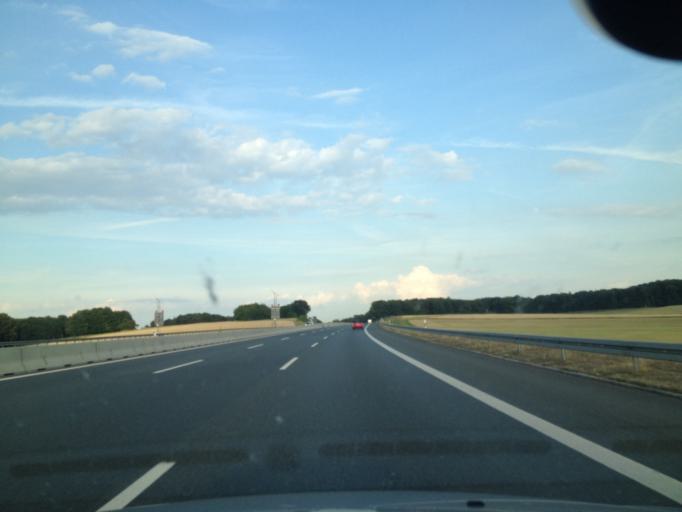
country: DE
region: Bavaria
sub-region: Regierungsbezirk Unterfranken
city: Uettingen
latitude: 49.7749
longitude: 9.7356
